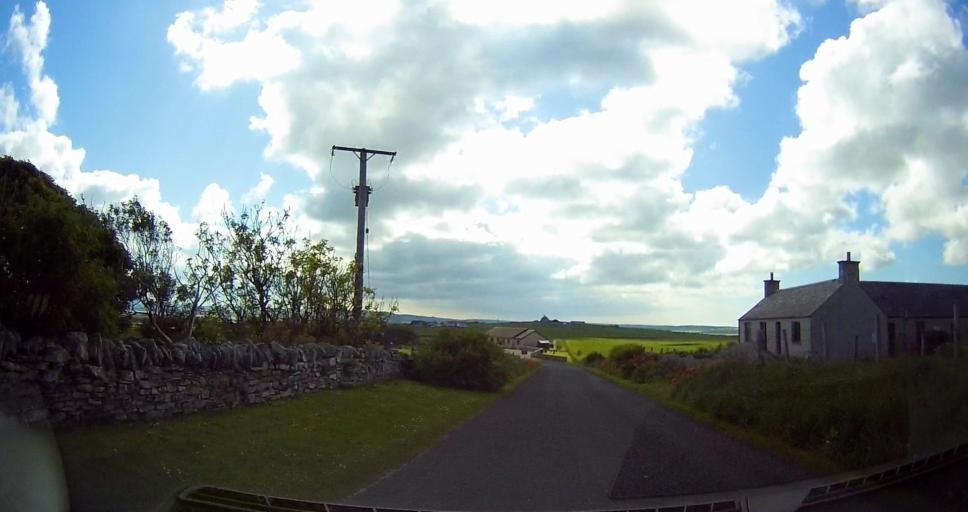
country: GB
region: Scotland
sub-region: Orkney Islands
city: Stromness
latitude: 59.0442
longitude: -3.1805
